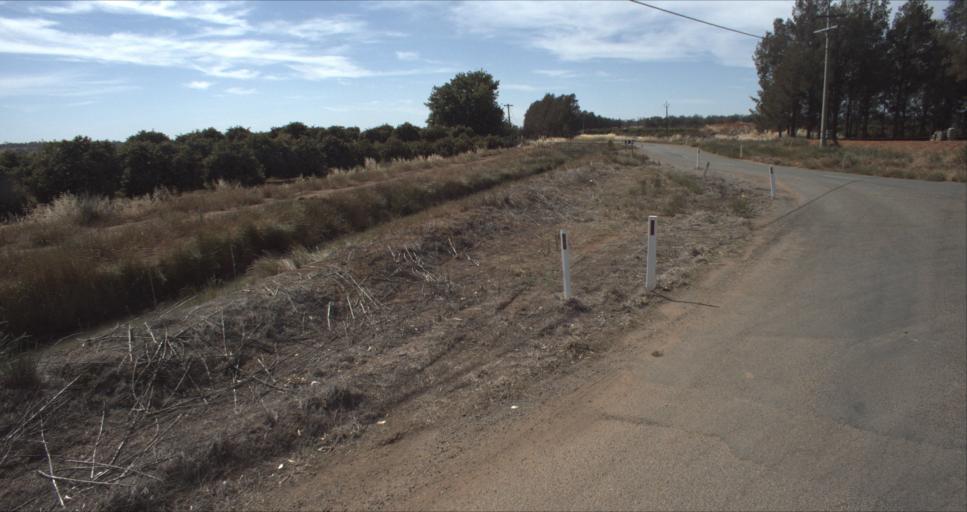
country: AU
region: New South Wales
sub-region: Leeton
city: Leeton
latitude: -34.5910
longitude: 146.4630
